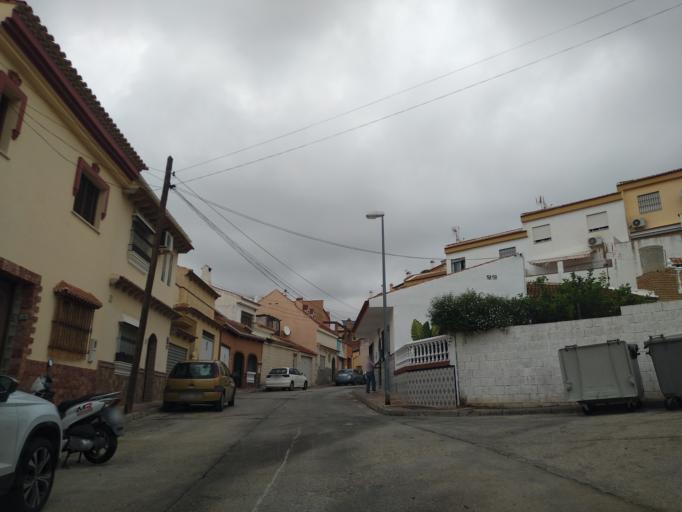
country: ES
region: Andalusia
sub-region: Provincia de Malaga
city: Malaga
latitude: 36.7433
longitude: -4.4781
